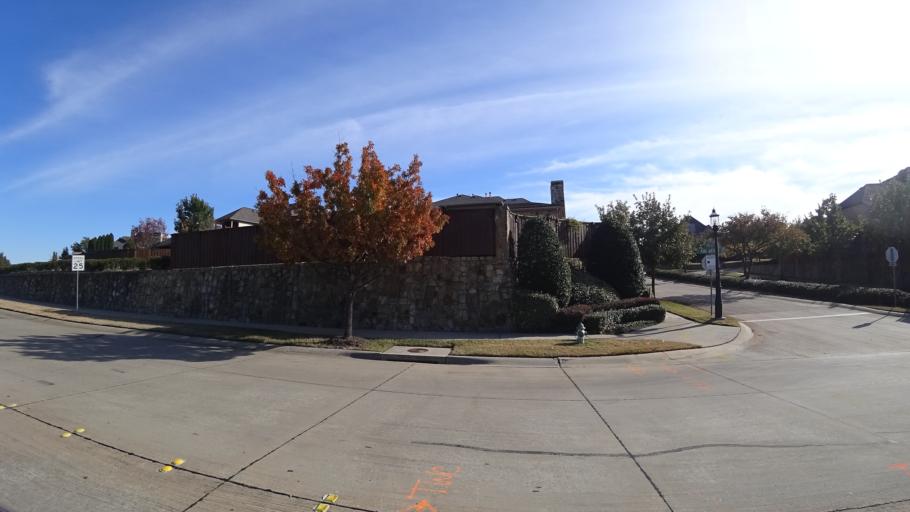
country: US
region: Texas
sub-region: Denton County
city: The Colony
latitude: 33.0303
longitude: -96.9115
